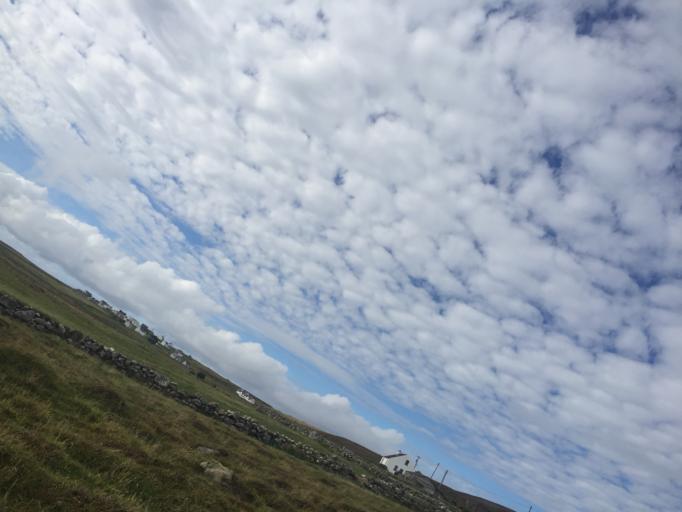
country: IE
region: Ulster
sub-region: County Donegal
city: Derrybeg
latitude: 55.2547
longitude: -8.1954
